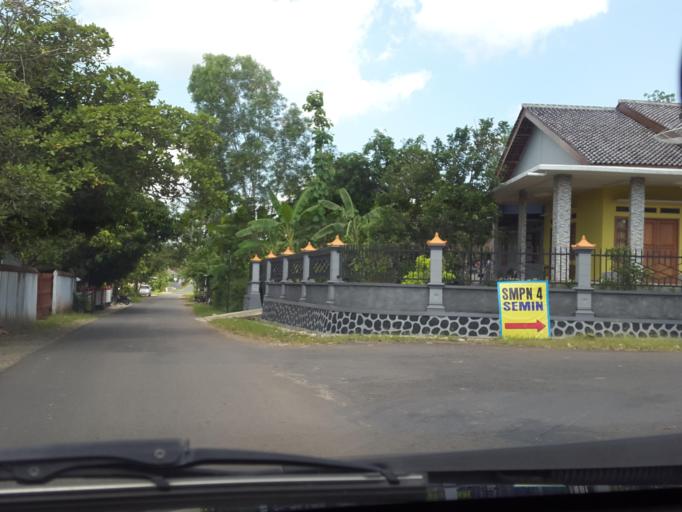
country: ID
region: Central Java
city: Selogiri
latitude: -7.8660
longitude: 110.7438
